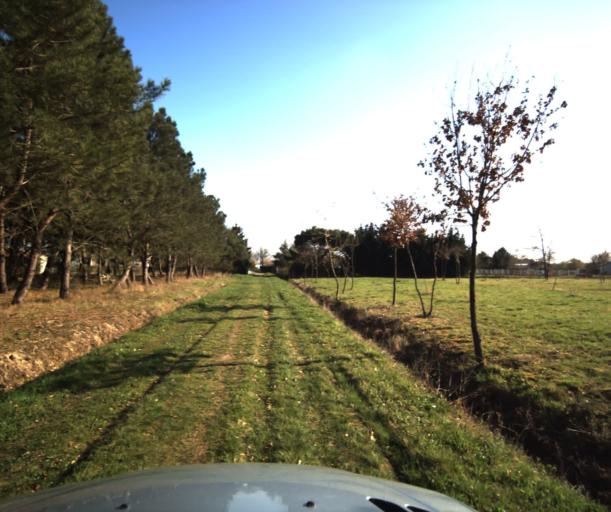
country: FR
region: Midi-Pyrenees
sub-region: Departement du Tarn-et-Garonne
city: Bressols
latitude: 43.9400
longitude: 1.3140
